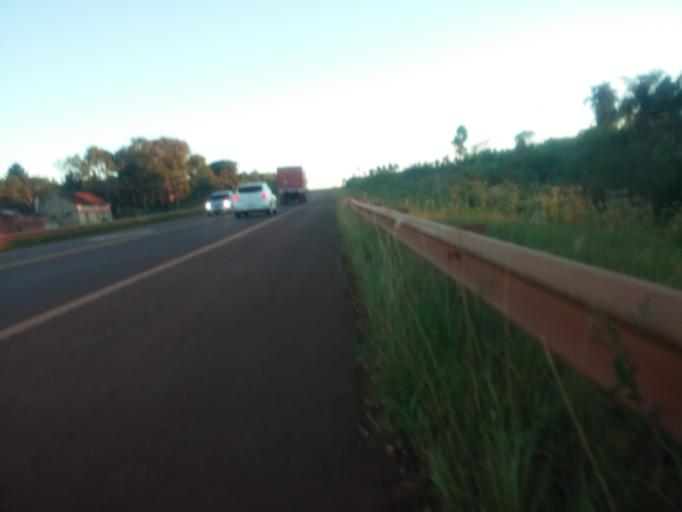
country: AR
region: Misiones
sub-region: Departamento de Obera
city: Obera
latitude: -27.4382
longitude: -55.0829
